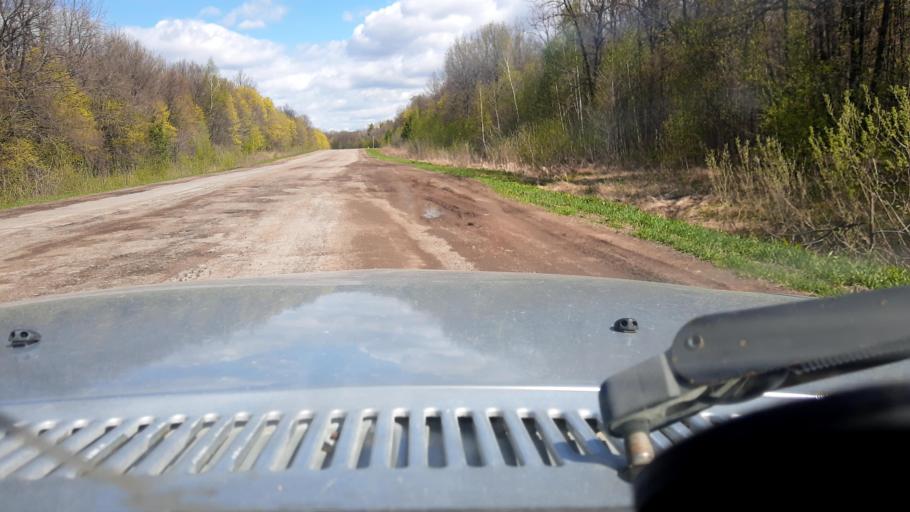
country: RU
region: Bashkortostan
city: Blagoveshchensk
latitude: 55.0823
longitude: 56.0551
